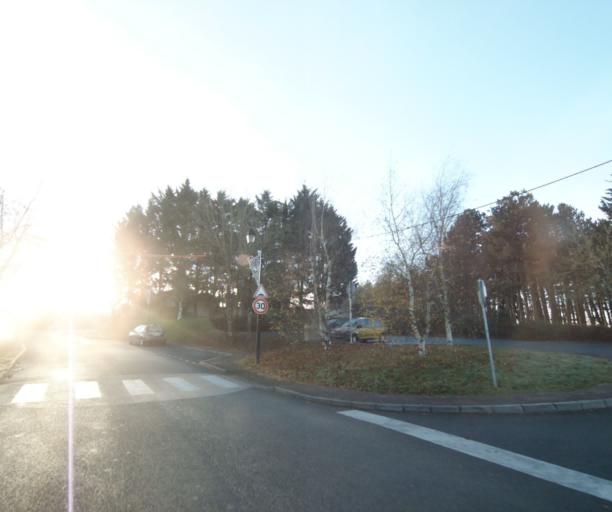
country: FR
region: Poitou-Charentes
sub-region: Departement de la Charente-Maritime
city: Fontcouverte
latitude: 45.7704
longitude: -0.5913
